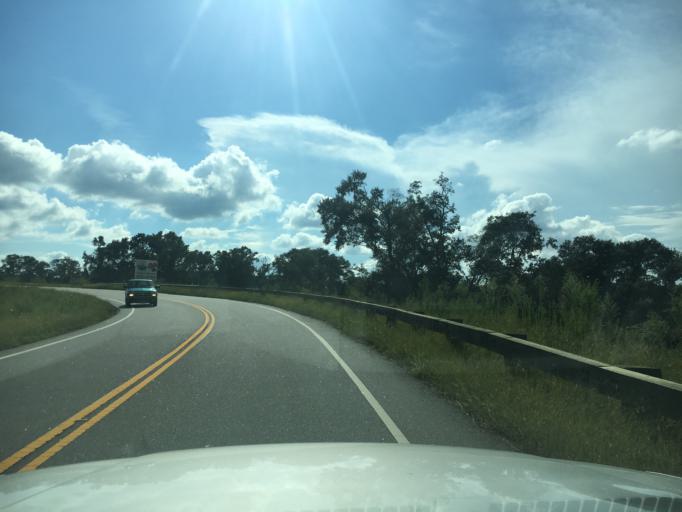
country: US
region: South Carolina
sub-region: Spartanburg County
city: Roebuck
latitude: 34.8840
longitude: -82.0131
